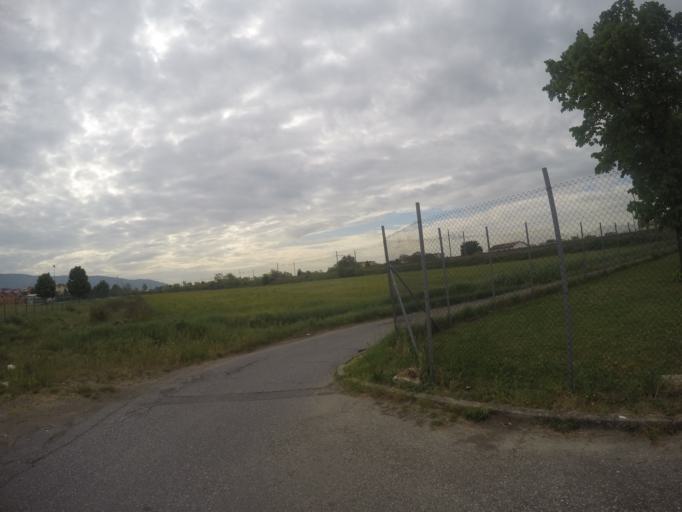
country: IT
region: Tuscany
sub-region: Provincia di Prato
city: Fornacelle
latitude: 43.8958
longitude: 11.0542
